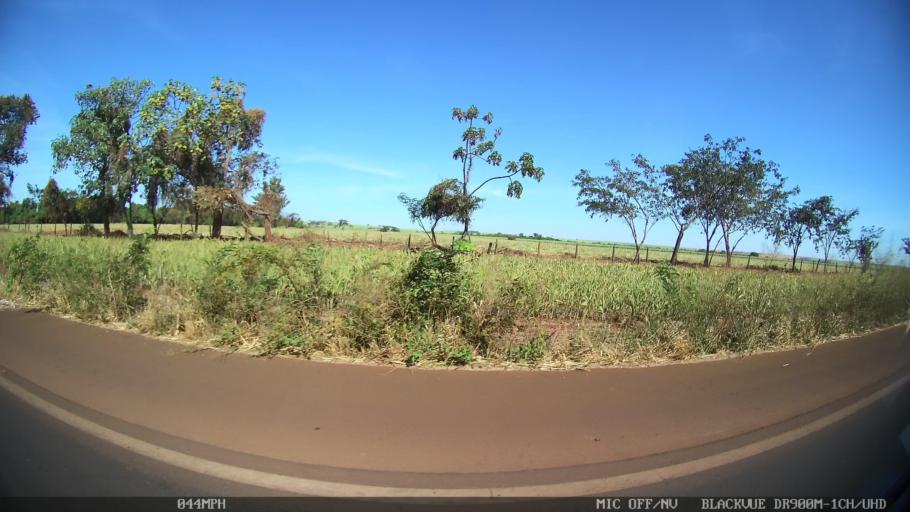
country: BR
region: Sao Paulo
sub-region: Ipua
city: Ipua
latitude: -20.5048
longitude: -47.9343
